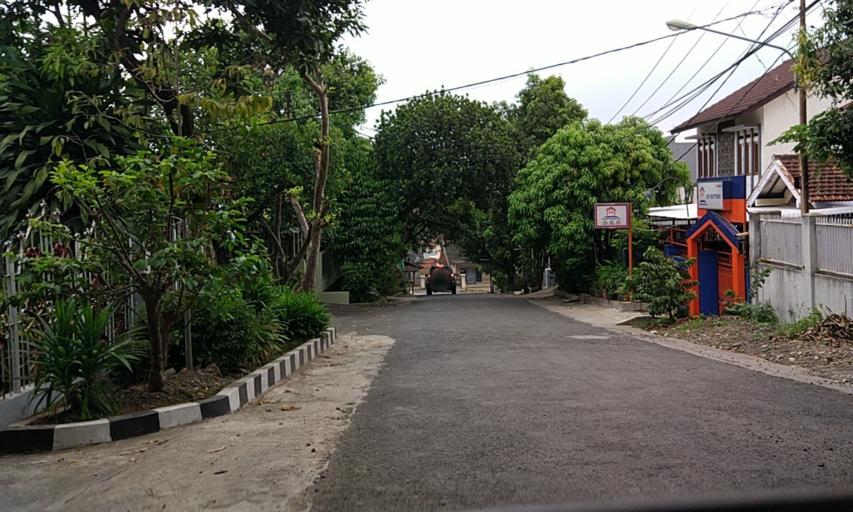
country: ID
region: West Java
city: Cileunyi
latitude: -6.9058
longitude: 107.6962
